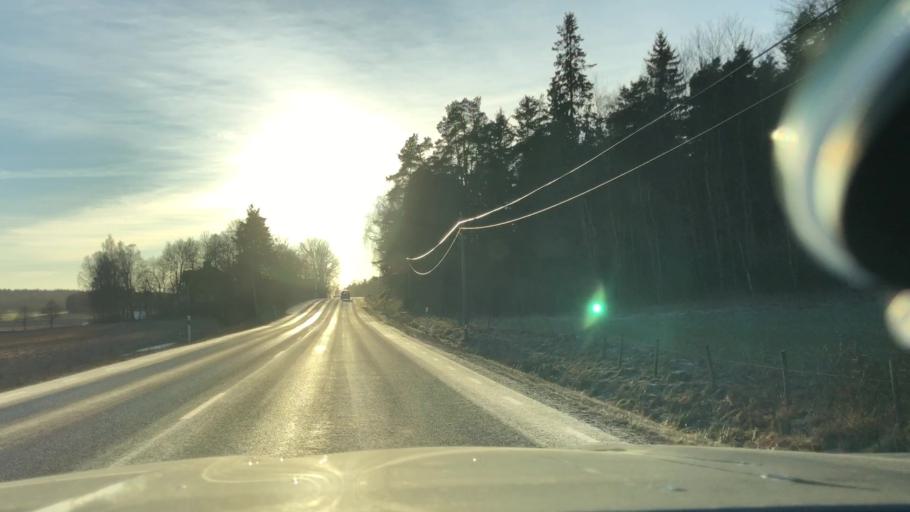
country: SE
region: Soedermanland
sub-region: Trosa Kommun
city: Vagnharad
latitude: 59.0376
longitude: 17.6007
